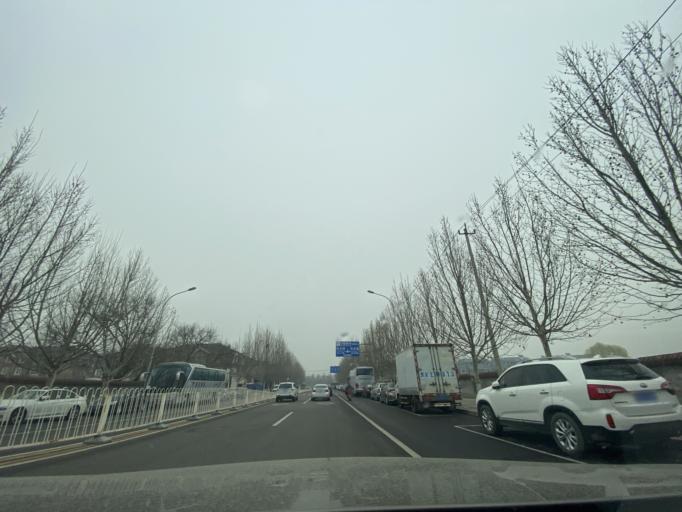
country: CN
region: Beijing
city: Sijiqing
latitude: 39.9696
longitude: 116.2404
